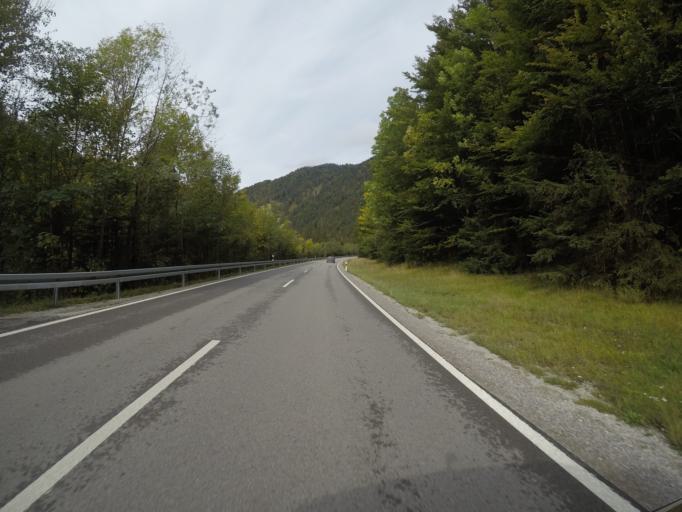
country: AT
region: Tyrol
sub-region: Politischer Bezirk Schwaz
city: Achenkirch
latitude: 47.5817
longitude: 11.6290
